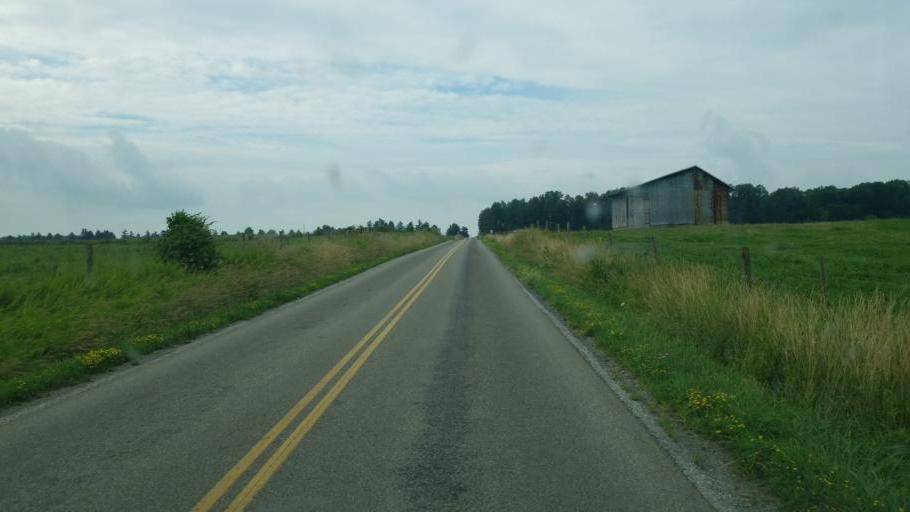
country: US
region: Ohio
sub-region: Wayne County
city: Apple Creek
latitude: 40.7654
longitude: -81.8241
